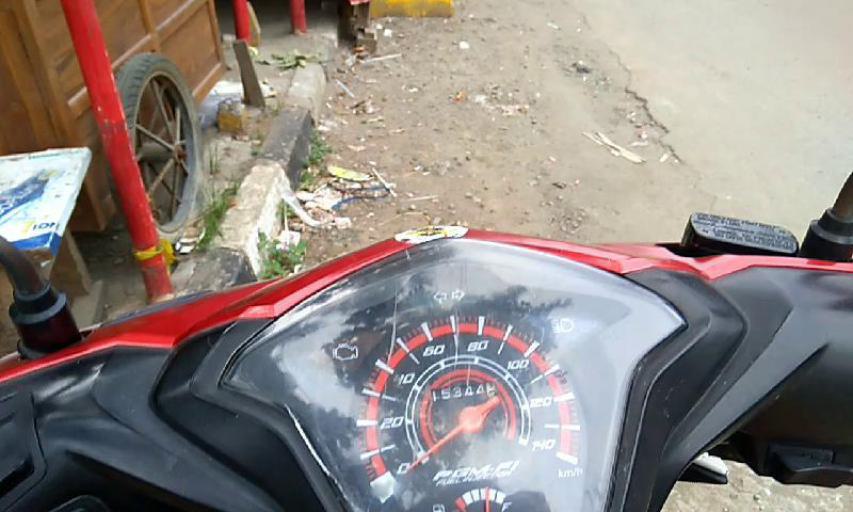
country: ID
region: West Java
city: Bekasi
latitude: -6.1976
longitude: 106.9851
